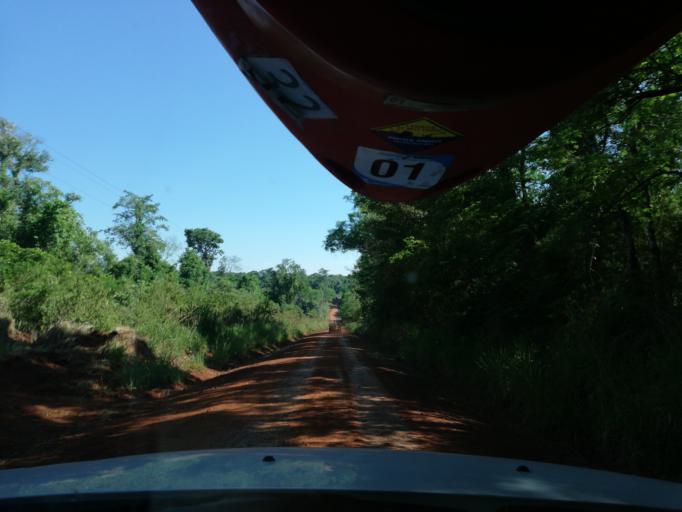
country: AR
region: Misiones
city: Puerto Leoni
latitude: -26.9731
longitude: -55.1646
